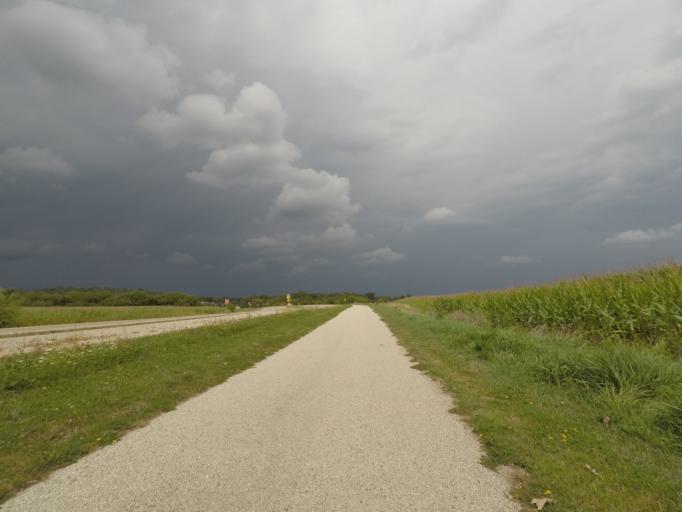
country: US
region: Wisconsin
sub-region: Jefferson County
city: Fort Atkinson
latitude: 42.9486
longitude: -88.8271
